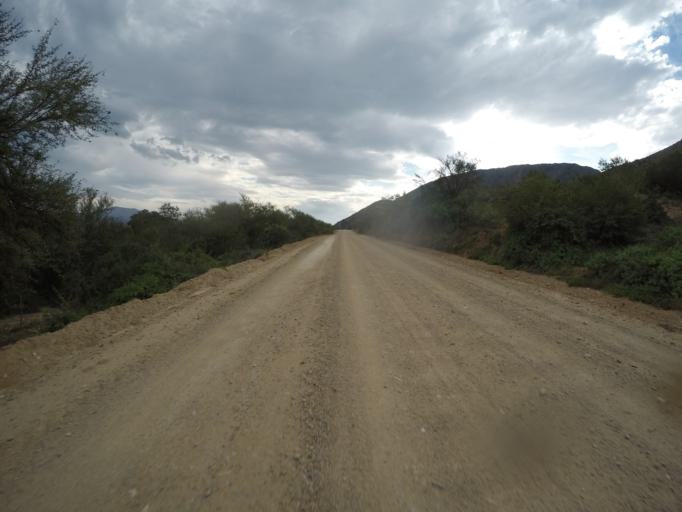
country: ZA
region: Eastern Cape
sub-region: Cacadu District Municipality
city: Kareedouw
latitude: -33.5722
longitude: 24.1260
